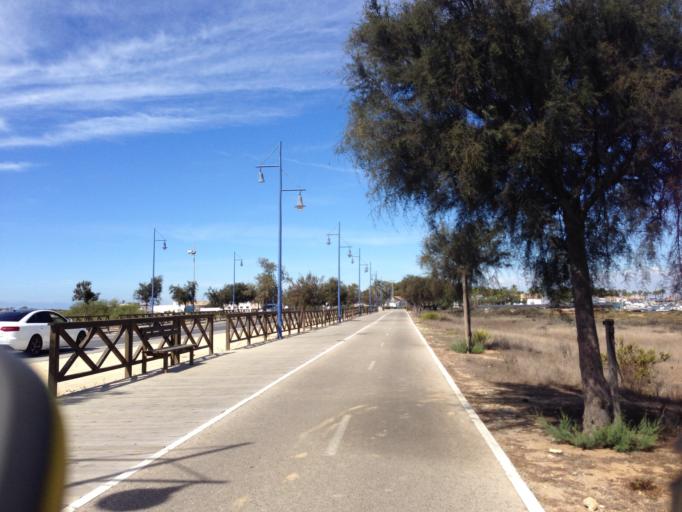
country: ES
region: Andalusia
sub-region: Provincia de Cadiz
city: Chiclana de la Frontera
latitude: 36.3906
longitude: -6.2072
